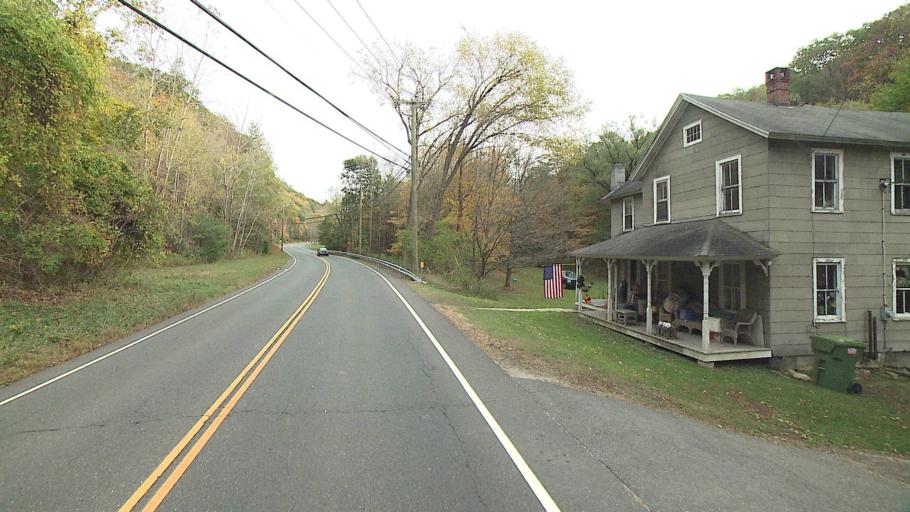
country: US
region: Connecticut
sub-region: Litchfield County
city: Canaan
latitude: 42.0021
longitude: -73.2218
